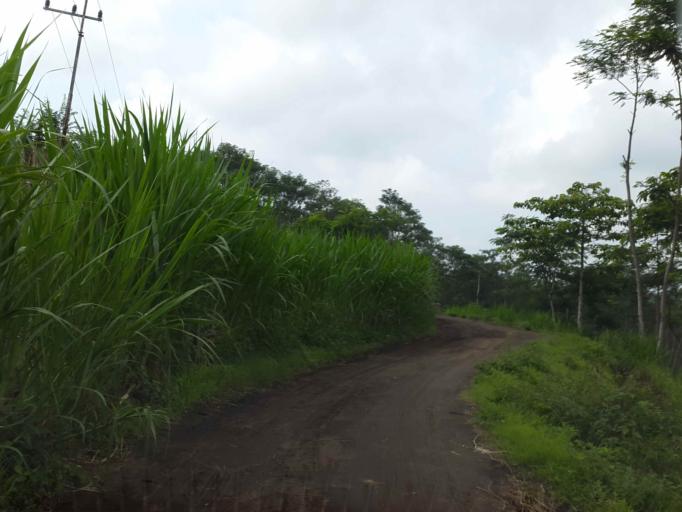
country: ID
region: East Java
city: Pandansari
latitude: -8.0898
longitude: 112.7928
